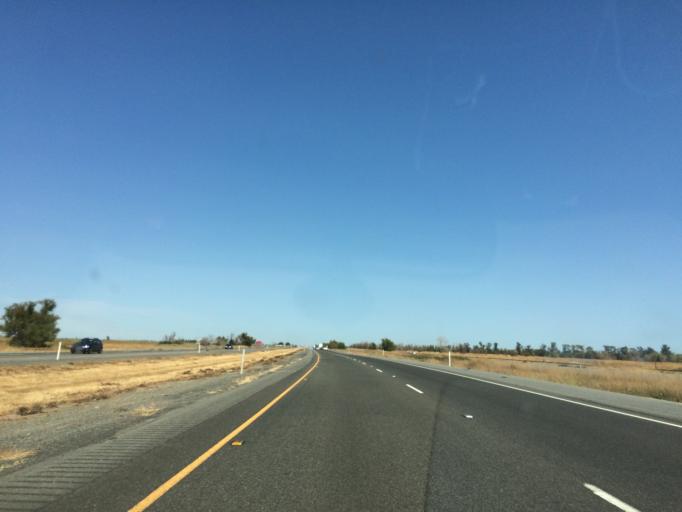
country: US
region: California
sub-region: Glenn County
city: Willows
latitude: 39.4197
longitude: -122.1932
